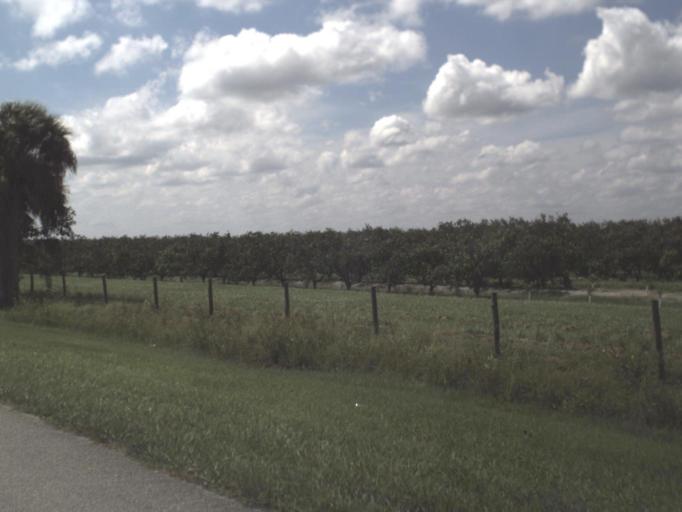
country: US
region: Florida
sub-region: Collier County
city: Immokalee
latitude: 26.5388
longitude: -81.4355
